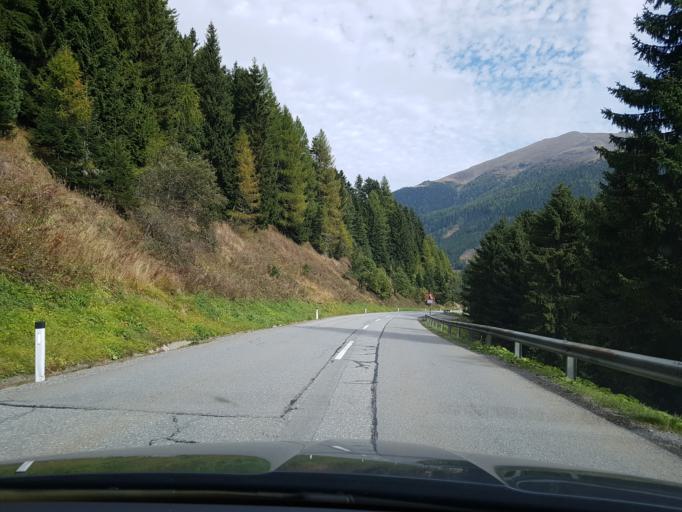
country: AT
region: Salzburg
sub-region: Politischer Bezirk Tamsweg
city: Ramingstein
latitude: 46.9352
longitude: 13.8760
